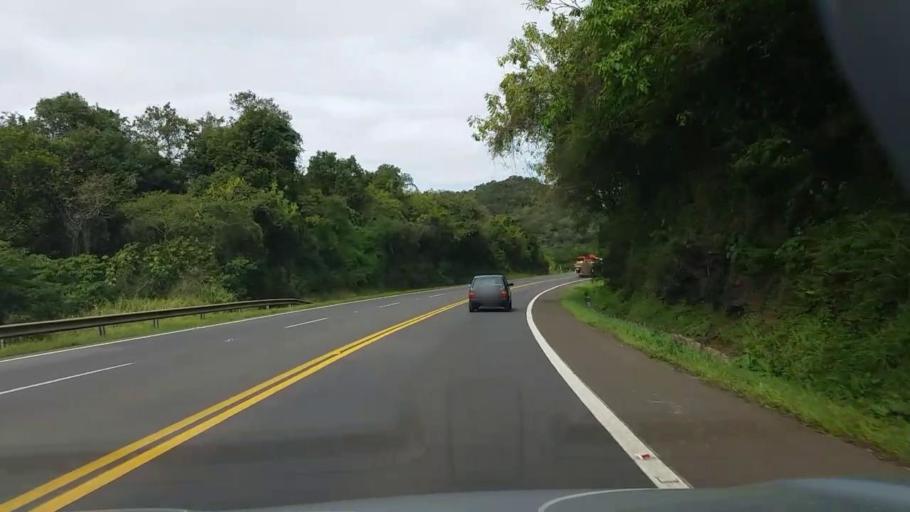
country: BR
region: Rio Grande do Sul
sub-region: Arroio Do Meio
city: Arroio do Meio
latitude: -29.3890
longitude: -52.0424
